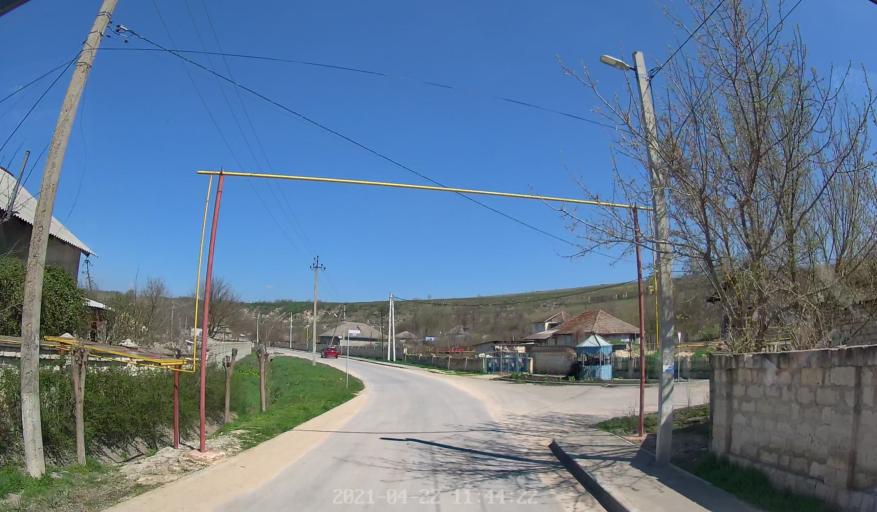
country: MD
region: Chisinau
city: Ciorescu
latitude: 47.1429
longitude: 28.8976
